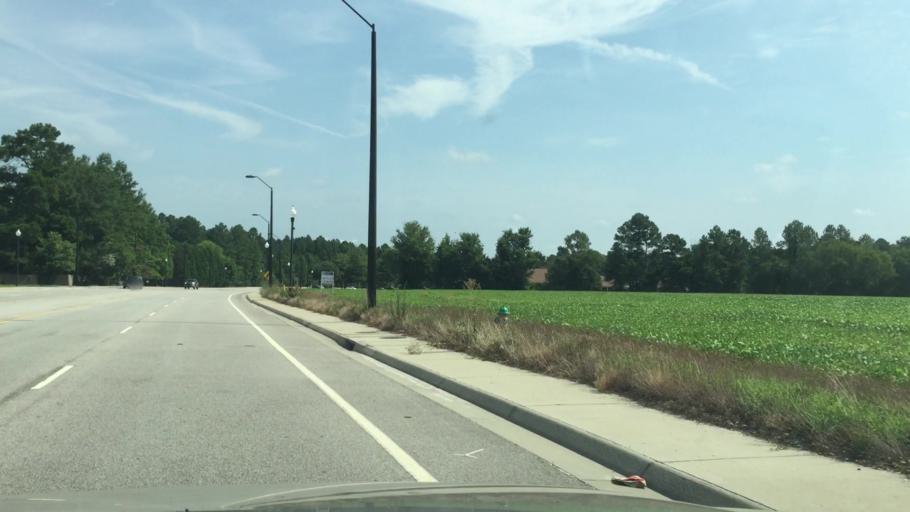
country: US
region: South Carolina
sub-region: Sumter County
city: Sumter
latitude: 33.9598
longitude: -80.3877
